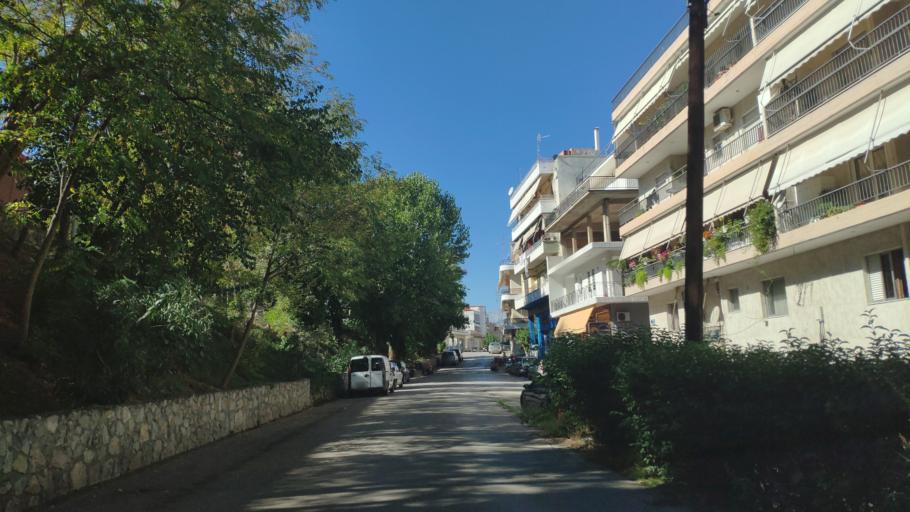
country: GR
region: Central Greece
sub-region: Nomos Voiotias
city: Livadeia
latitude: 38.4390
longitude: 22.8720
